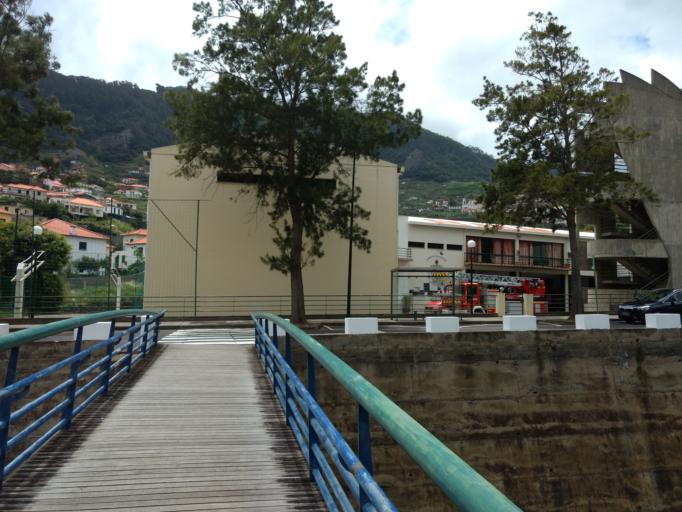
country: PT
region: Madeira
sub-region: Machico
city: Machico
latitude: 32.7296
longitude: -16.7753
